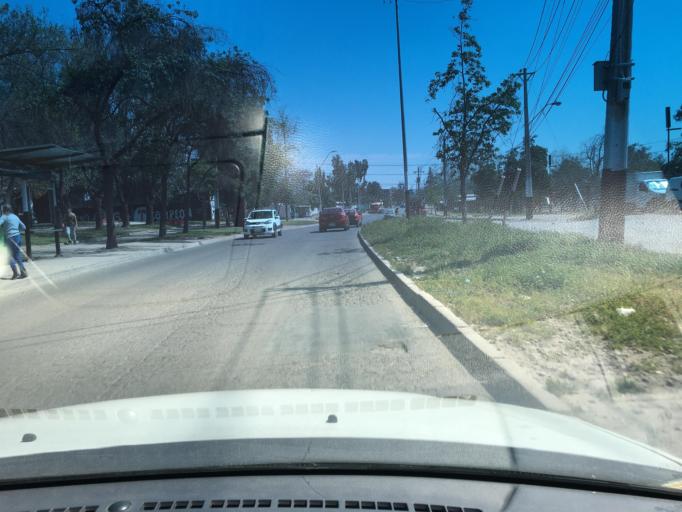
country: CL
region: Santiago Metropolitan
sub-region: Provincia de Santiago
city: Villa Presidente Frei, Nunoa, Santiago, Chile
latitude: -33.5175
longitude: -70.5554
